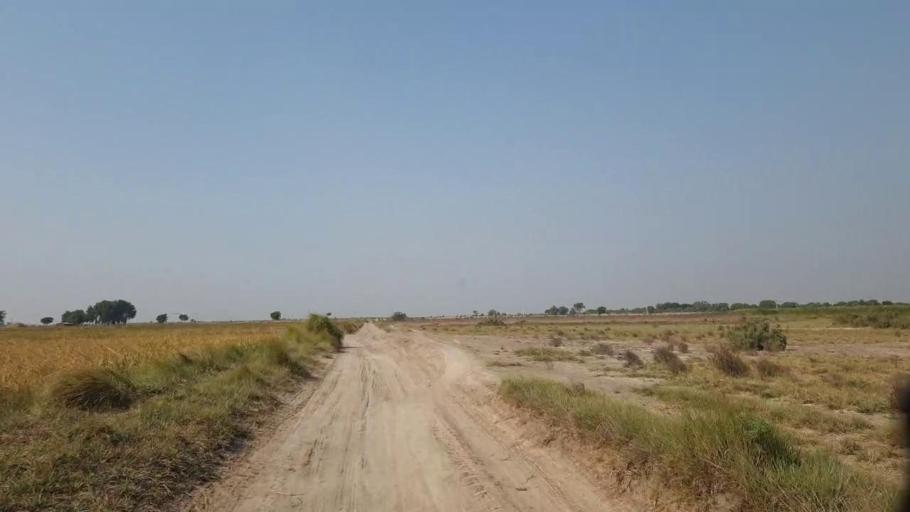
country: PK
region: Sindh
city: Bulri
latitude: 24.9479
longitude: 68.3802
